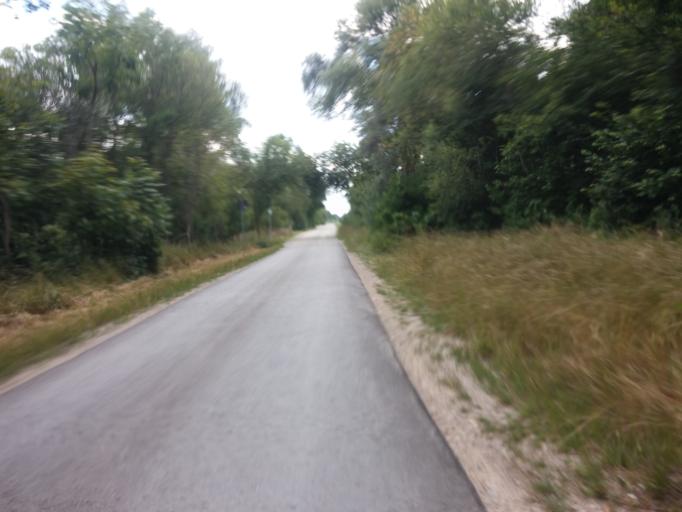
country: DE
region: Bavaria
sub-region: Upper Bavaria
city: Aschheim
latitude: 48.1767
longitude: 11.6940
